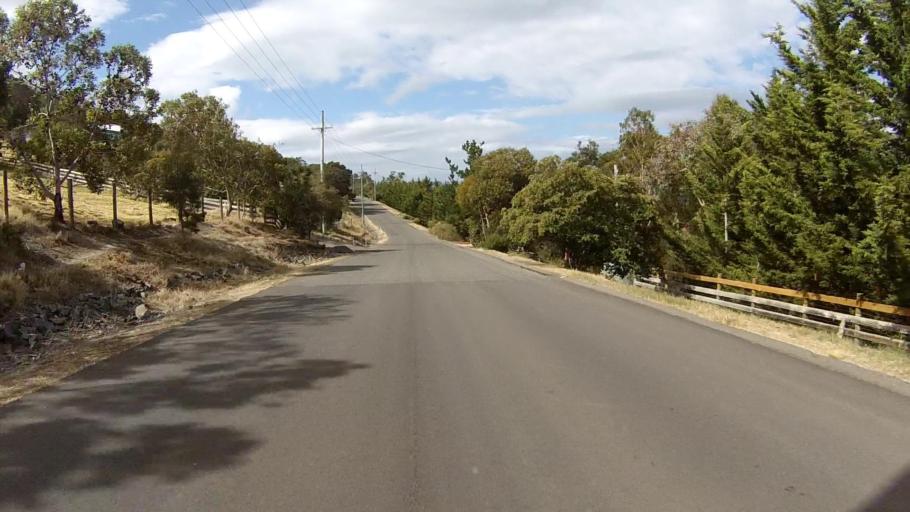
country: AU
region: Tasmania
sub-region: Clarence
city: Acton Park
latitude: -42.8835
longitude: 147.5031
